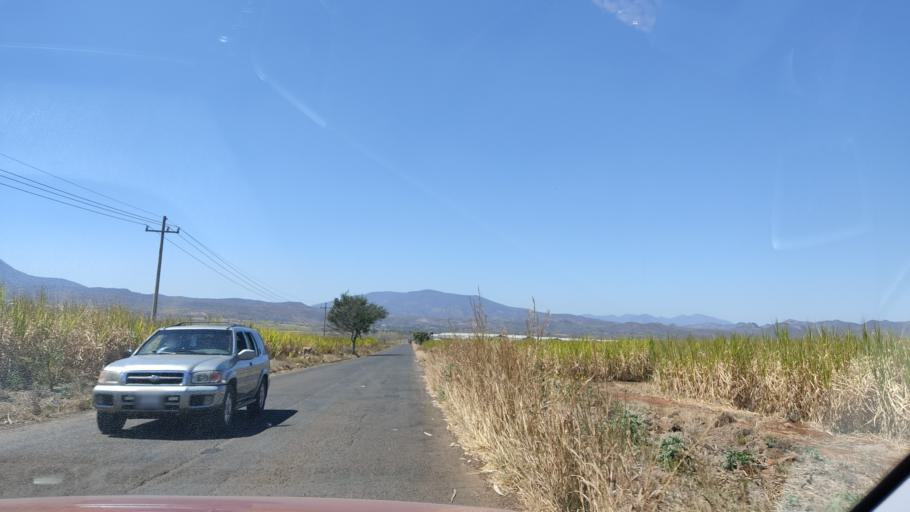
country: MX
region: Nayarit
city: Santa Maria del Oro
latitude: 21.4338
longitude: -104.6177
